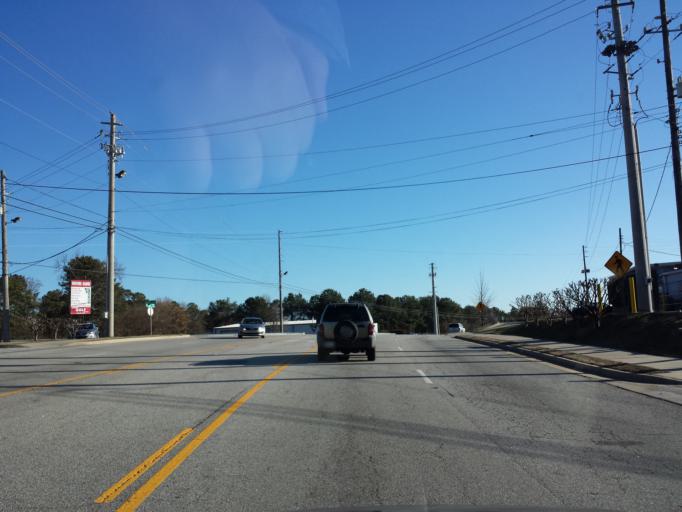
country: US
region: Georgia
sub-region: Cobb County
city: Marietta
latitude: 33.9591
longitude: -84.5139
